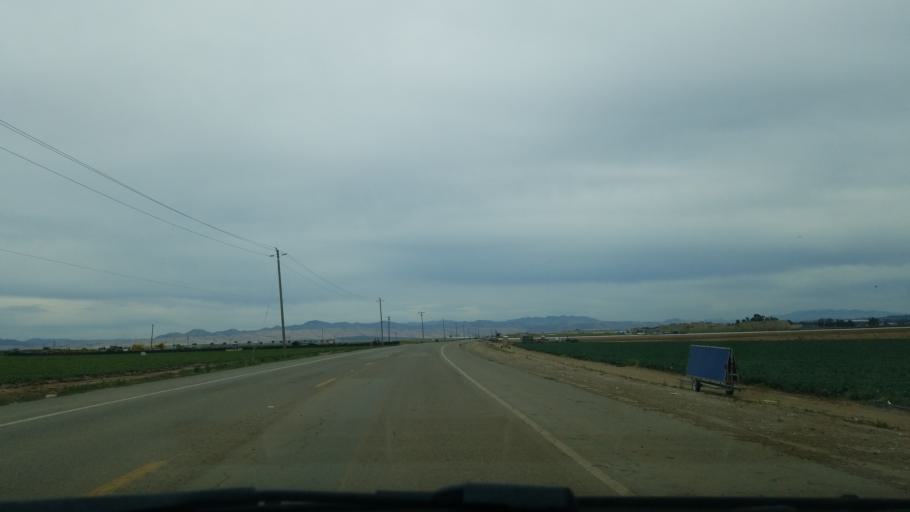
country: US
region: California
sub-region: Santa Barbara County
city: Santa Maria
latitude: 34.9202
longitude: -120.5014
